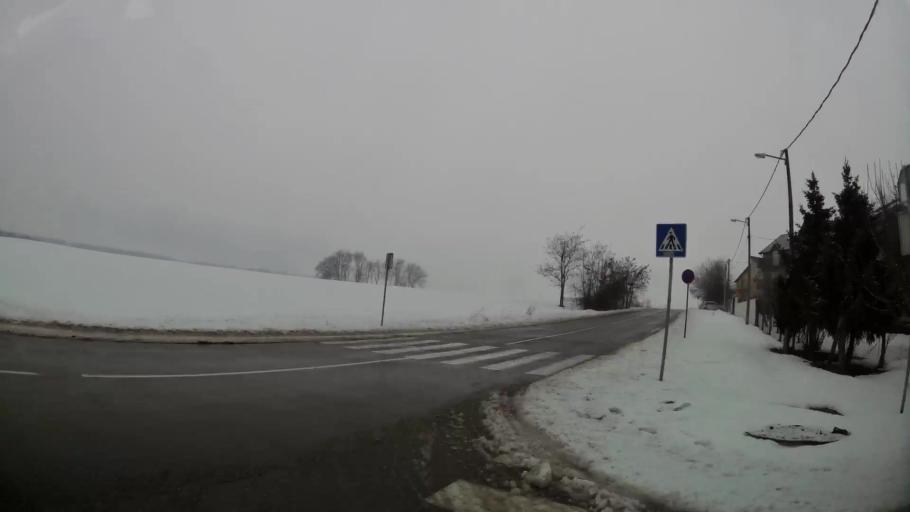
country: RS
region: Central Serbia
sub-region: Belgrade
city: Zemun
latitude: 44.8453
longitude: 20.3478
